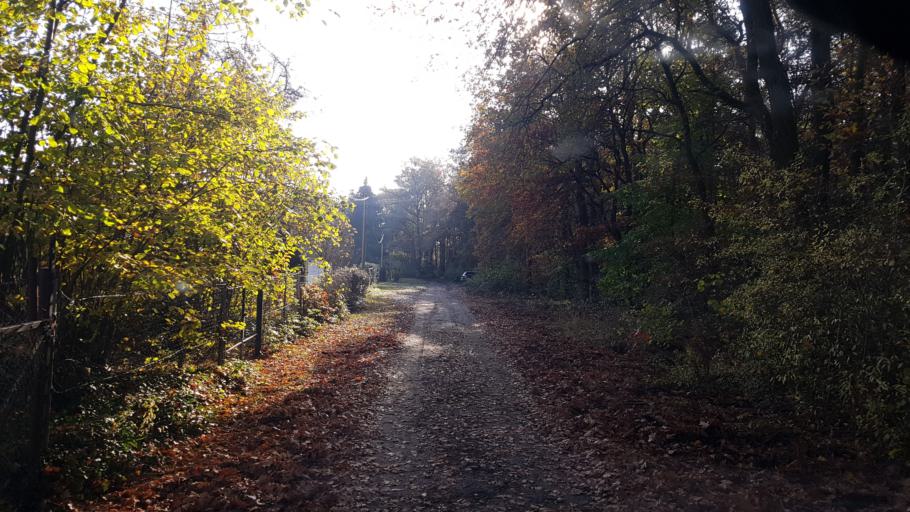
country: DE
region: Brandenburg
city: Schipkau
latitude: 51.5599
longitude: 13.9116
